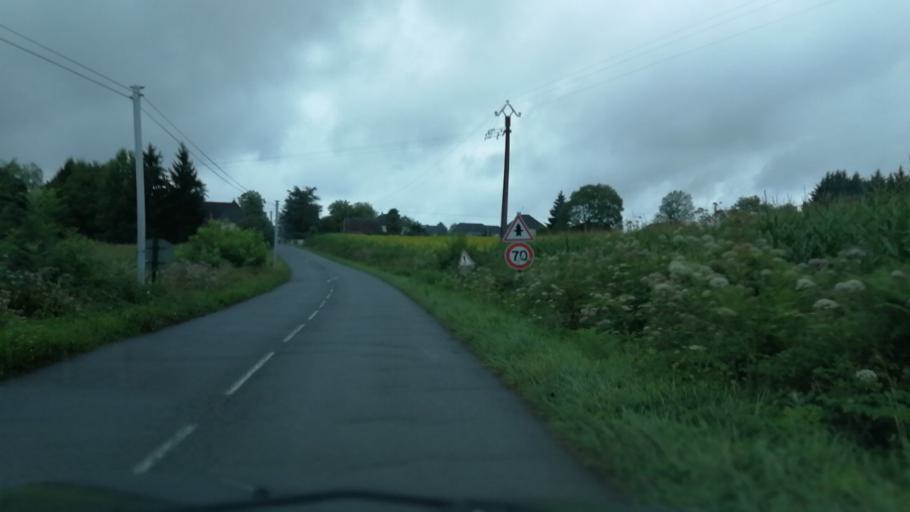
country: FR
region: Aquitaine
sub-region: Departement des Pyrenees-Atlantiques
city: Lucq-de-Bearn
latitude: 43.2943
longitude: -0.6673
